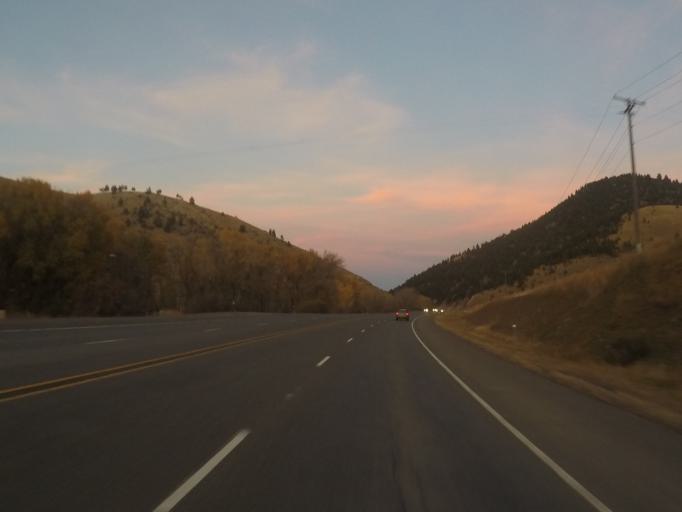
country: US
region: Montana
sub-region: Lewis and Clark County
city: Helena West Side
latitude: 46.5873
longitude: -112.1289
